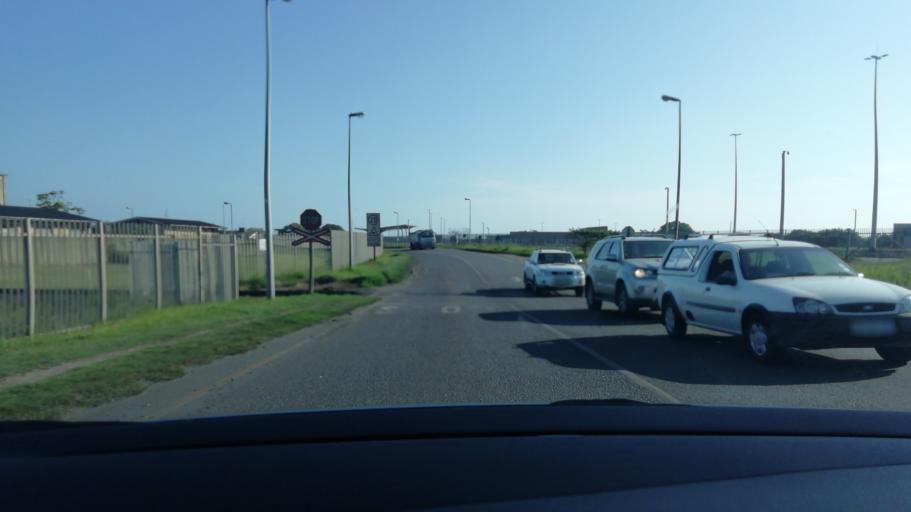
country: ZA
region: KwaZulu-Natal
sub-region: uThungulu District Municipality
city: Richards Bay
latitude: -28.7854
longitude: 32.0270
